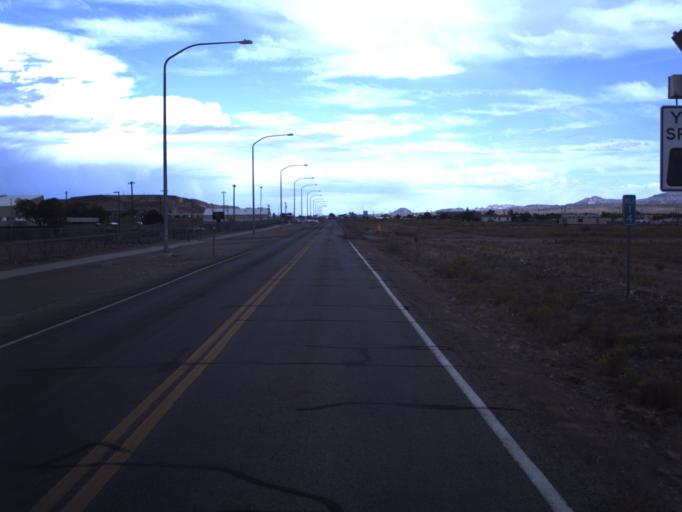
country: US
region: Utah
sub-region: San Juan County
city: Blanding
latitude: 37.2666
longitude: -109.3145
